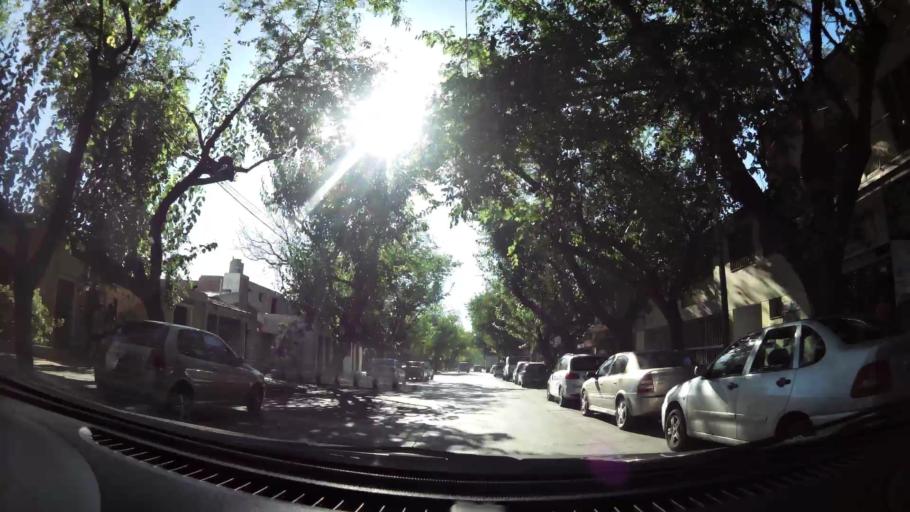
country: AR
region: Mendoza
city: Las Heras
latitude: -32.8688
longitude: -68.8496
